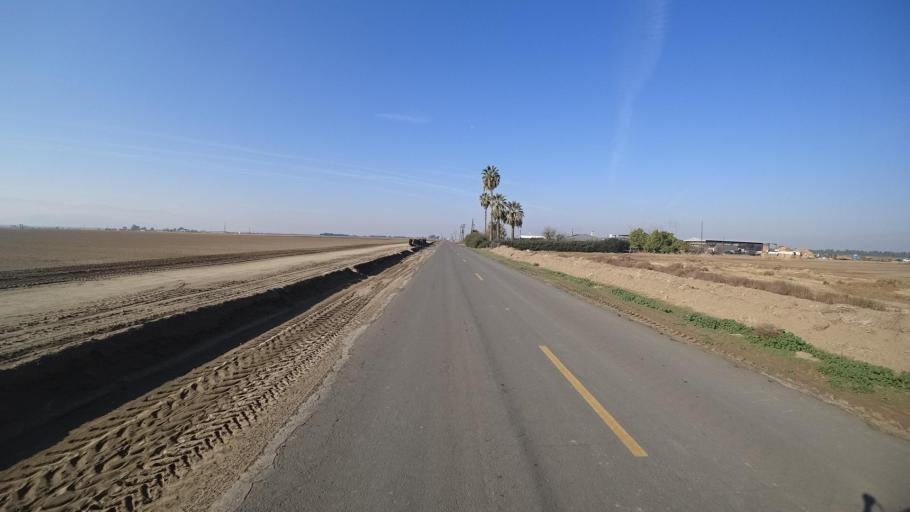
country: US
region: California
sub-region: Kern County
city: Arvin
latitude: 35.1218
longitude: -118.8979
